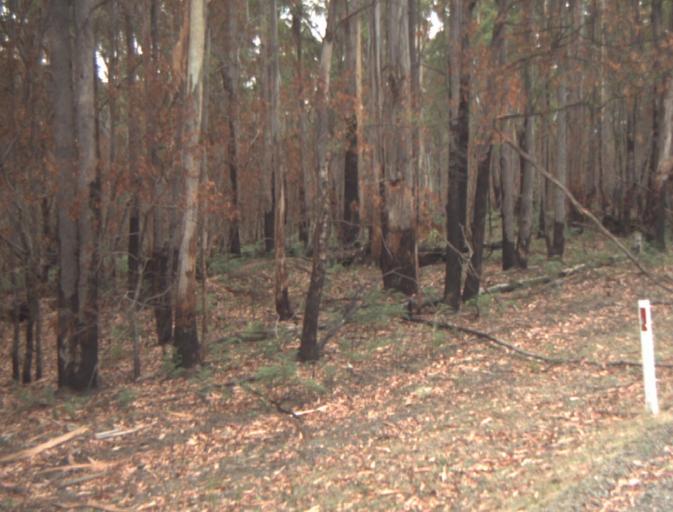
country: AU
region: Tasmania
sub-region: Dorset
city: Scottsdale
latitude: -41.4339
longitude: 147.5152
